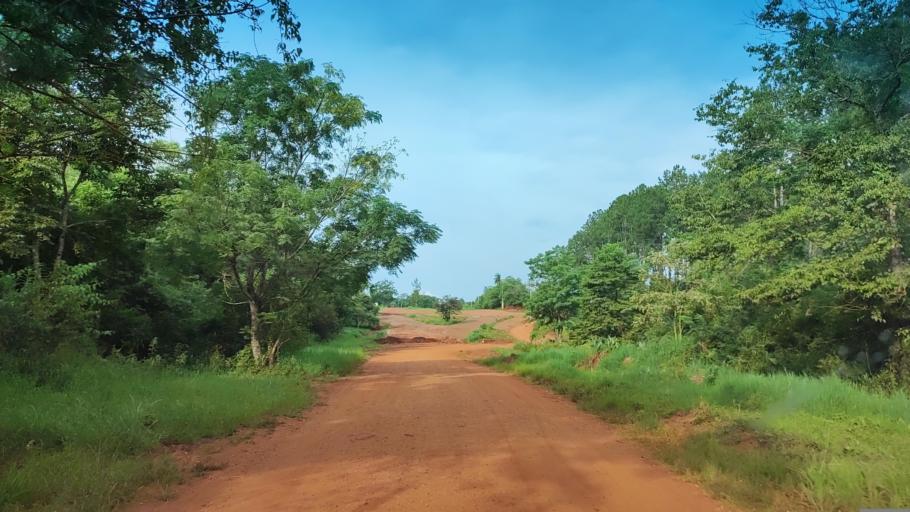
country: AR
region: Misiones
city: Gobernador Roca
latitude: -27.1373
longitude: -55.5195
